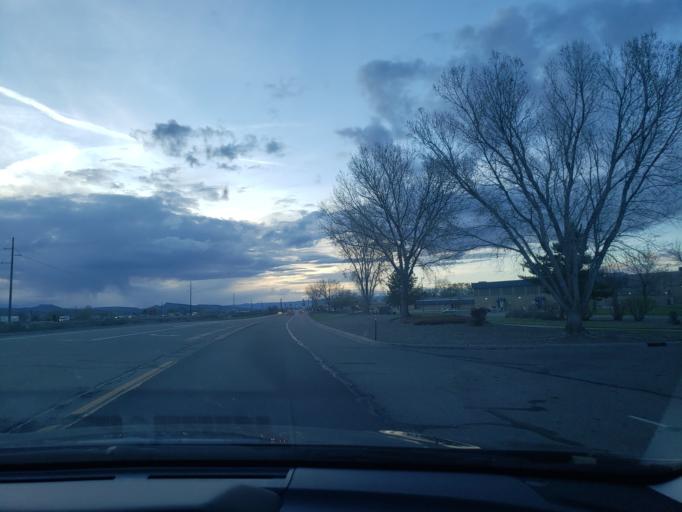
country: US
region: Colorado
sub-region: Mesa County
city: Fruita
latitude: 39.1465
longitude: -108.7157
